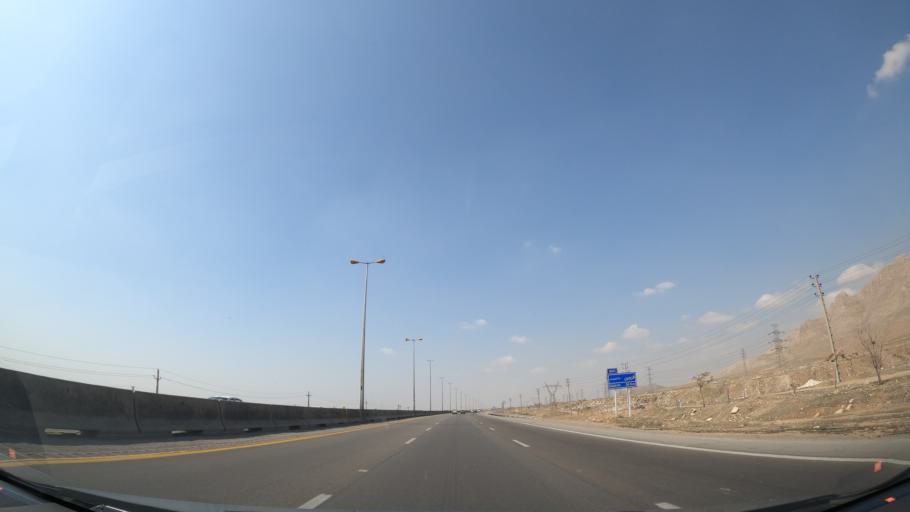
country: IR
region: Qazvin
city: Abyek
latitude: 36.0525
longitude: 50.5144
